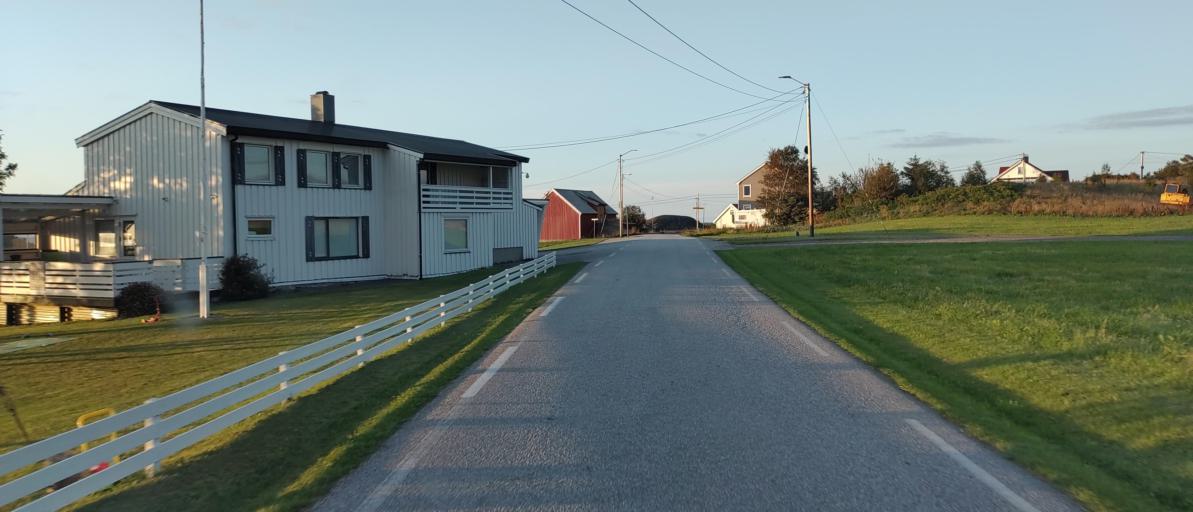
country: NO
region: More og Romsdal
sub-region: Fraena
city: Elnesvagen
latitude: 62.9966
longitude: 7.2229
